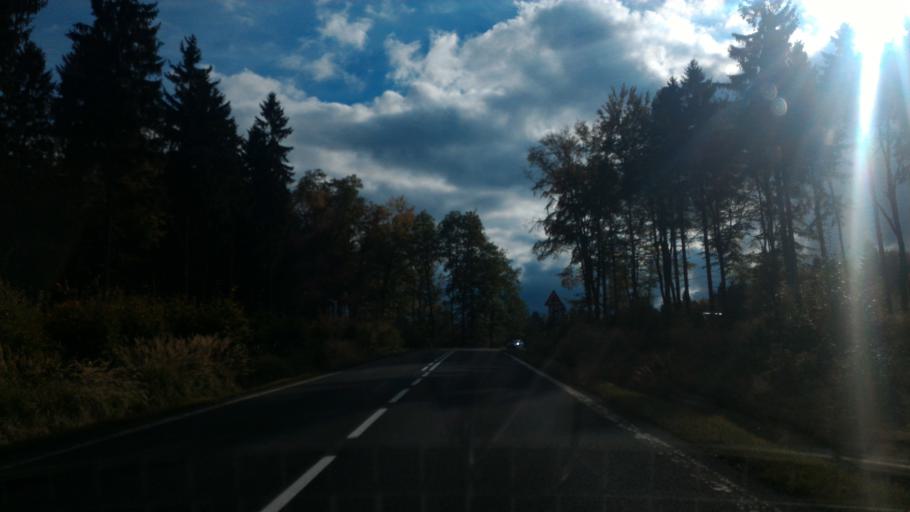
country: CZ
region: Ustecky
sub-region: Okres Decin
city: Chribska
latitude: 50.8336
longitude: 14.4914
